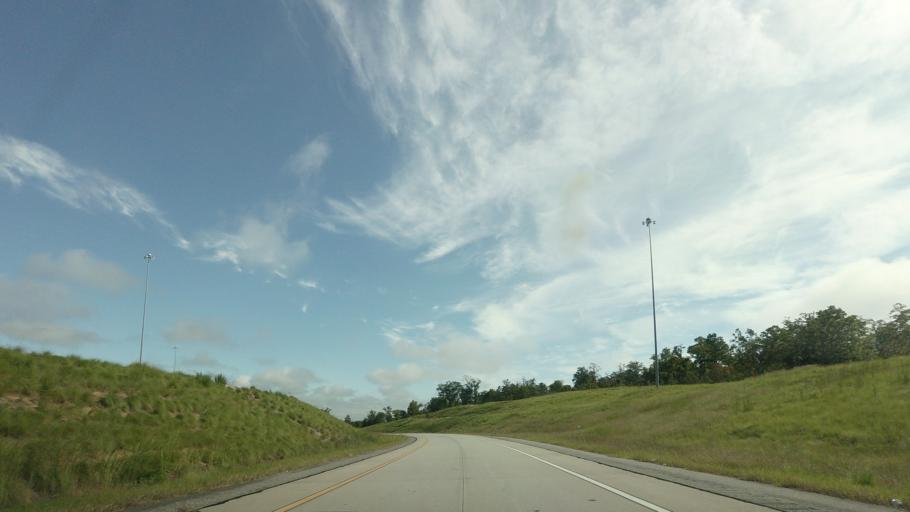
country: US
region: Georgia
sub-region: Bibb County
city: West Point
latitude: 32.7539
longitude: -83.7093
